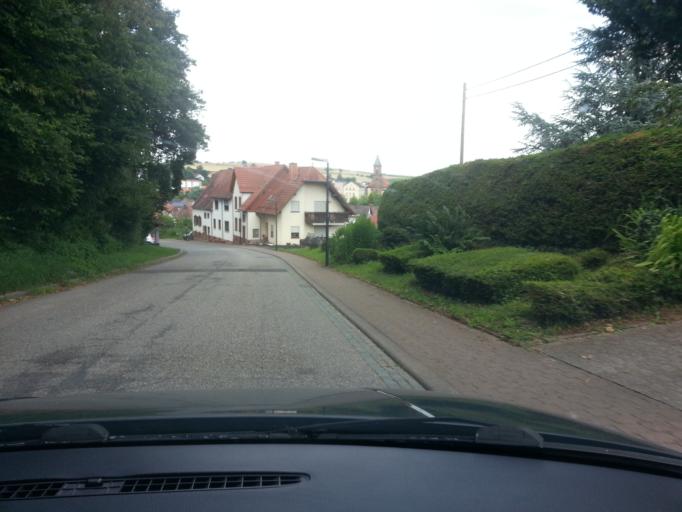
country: DE
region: Rheinland-Pfalz
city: Hornbach
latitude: 49.1853
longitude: 7.3643
